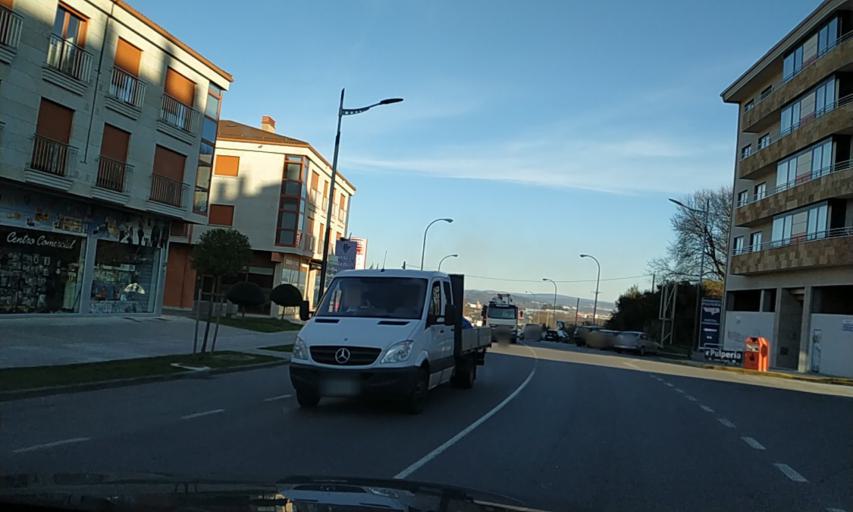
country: ES
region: Galicia
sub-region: Provincia de Pontevedra
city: Silleda
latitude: 42.6960
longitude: -8.2427
